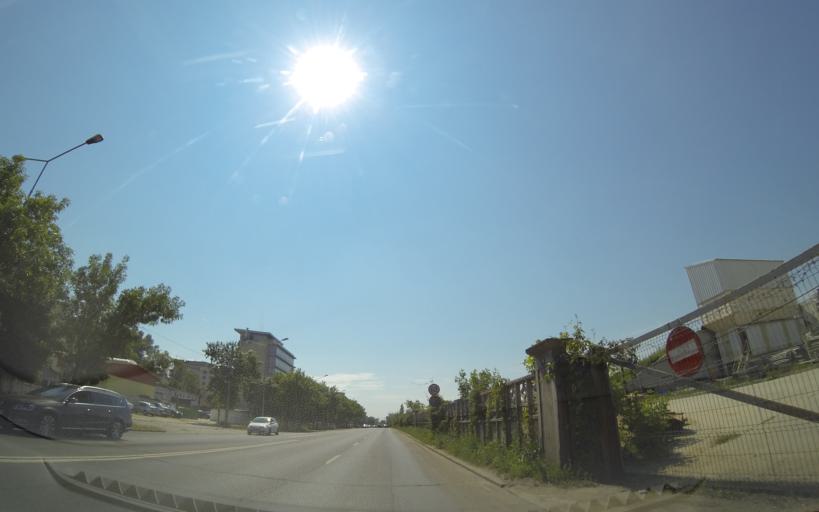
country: RO
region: Bucuresti
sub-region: Municipiul Bucuresti
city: Bucuresti
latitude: 44.4239
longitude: 26.0676
